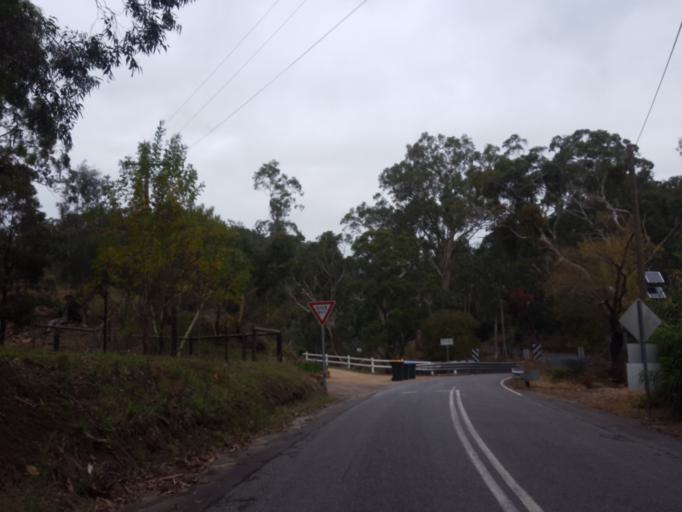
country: AU
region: South Australia
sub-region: Campbelltown
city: Athelstone
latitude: -34.8772
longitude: 138.7562
